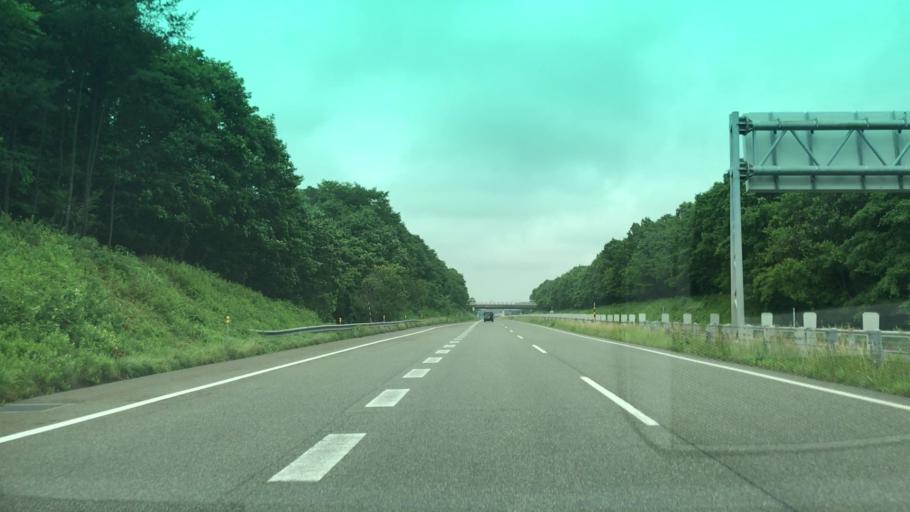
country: JP
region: Hokkaido
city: Tomakomai
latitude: 42.7133
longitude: 141.6522
